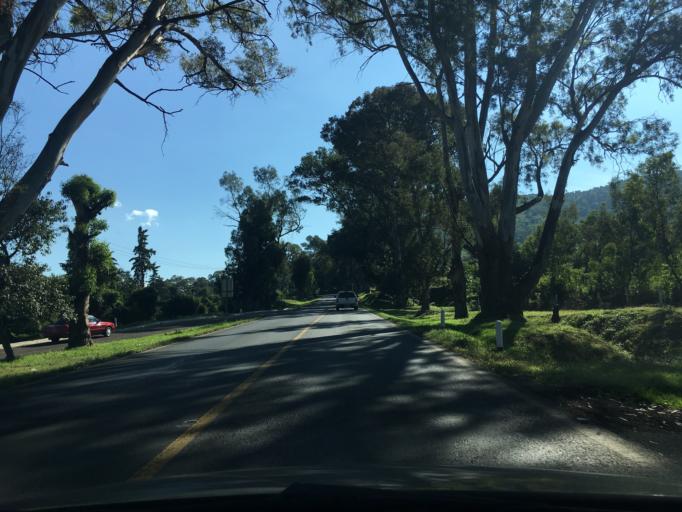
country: MX
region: Mexico
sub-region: Chalco
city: Zopoco
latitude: 19.8446
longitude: -102.0678
